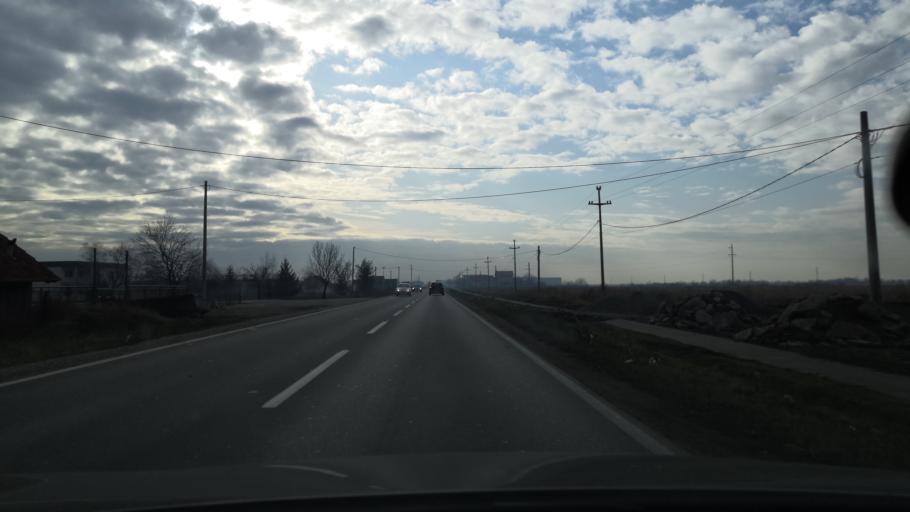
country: RS
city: Ugrinovci
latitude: 44.8654
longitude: 20.2044
